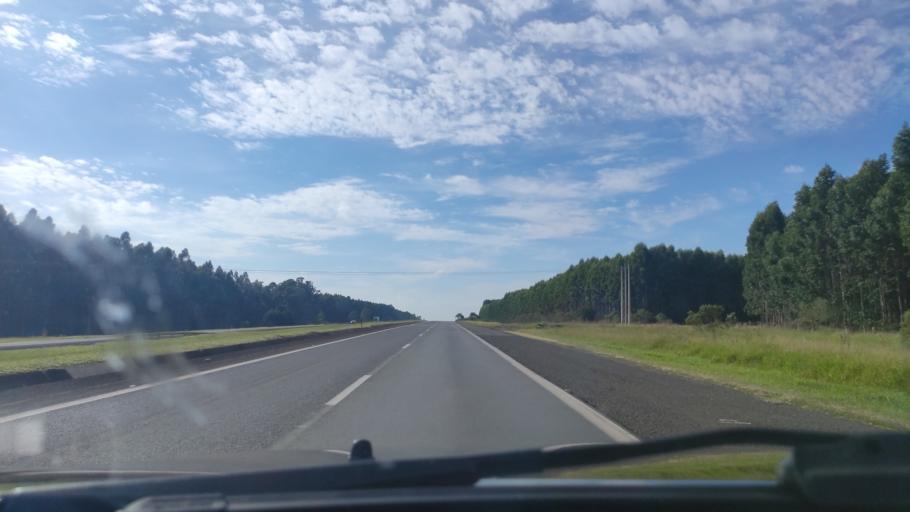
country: BR
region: Sao Paulo
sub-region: Itatinga
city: Itatinga
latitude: -23.0278
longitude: -48.6532
